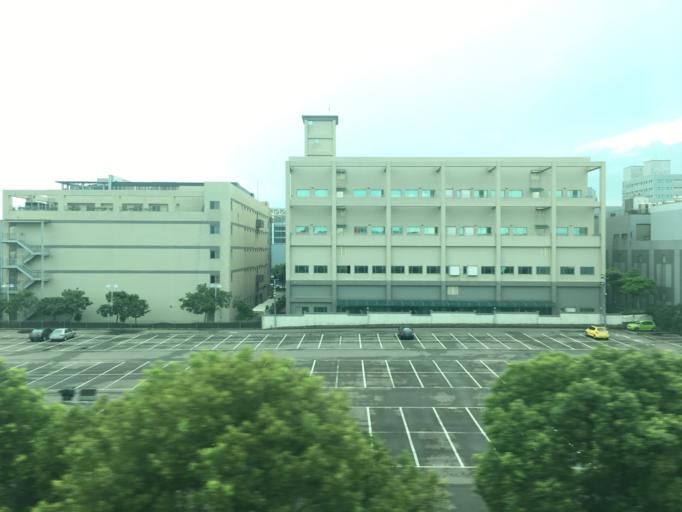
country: TW
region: Taiwan
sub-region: Taoyuan
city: Taoyuan
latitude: 25.0529
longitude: 121.3783
